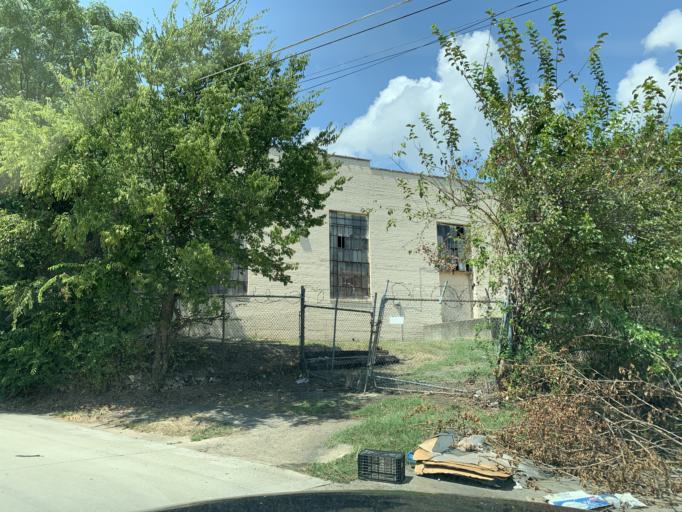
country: US
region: Texas
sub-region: Dallas County
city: Dallas
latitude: 32.7484
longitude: -96.8118
